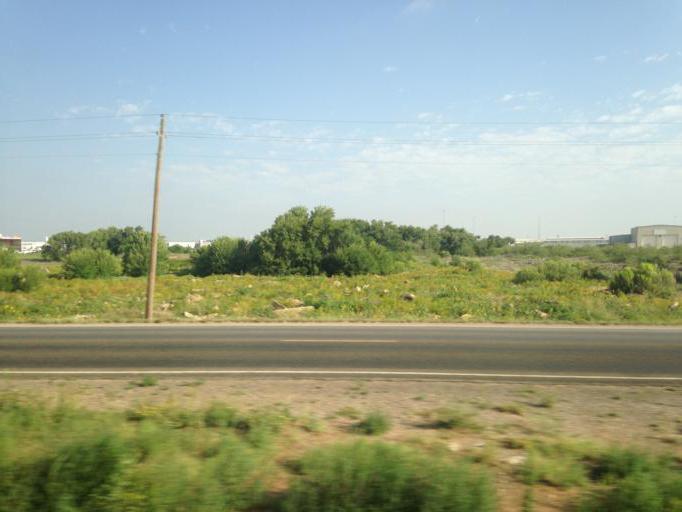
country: US
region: Texas
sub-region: Midland County
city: Midland
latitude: 31.9521
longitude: -102.1373
